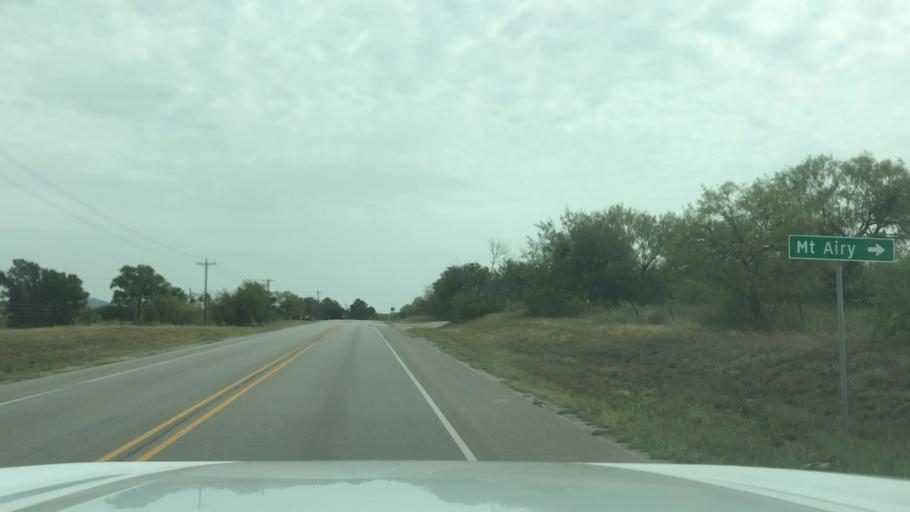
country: US
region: Texas
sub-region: Erath County
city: Dublin
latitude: 32.0946
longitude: -98.4113
